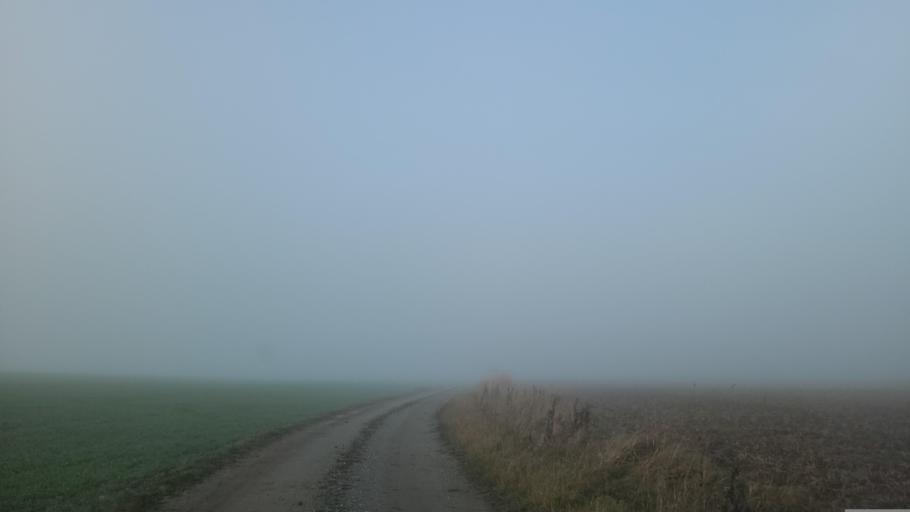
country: SE
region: Uppsala
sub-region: Enkopings Kommun
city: Grillby
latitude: 59.6027
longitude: 17.1738
